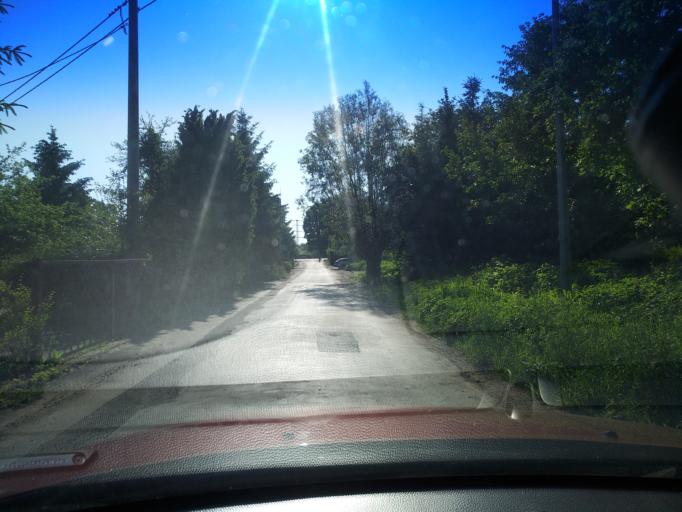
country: PL
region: Lower Silesian Voivodeship
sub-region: Powiat zgorzelecki
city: Zgorzelec
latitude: 51.1343
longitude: 15.0133
